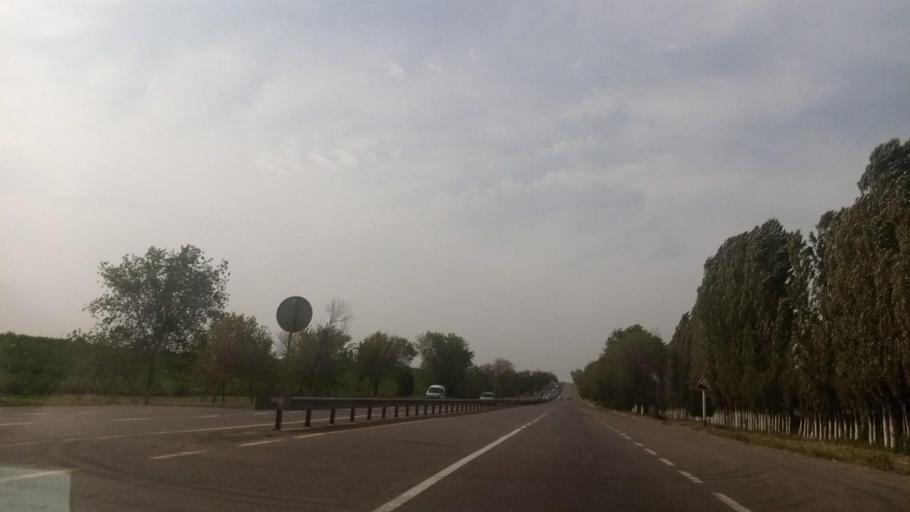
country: UZ
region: Toshkent
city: Tuytepa
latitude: 41.0913
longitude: 69.4626
